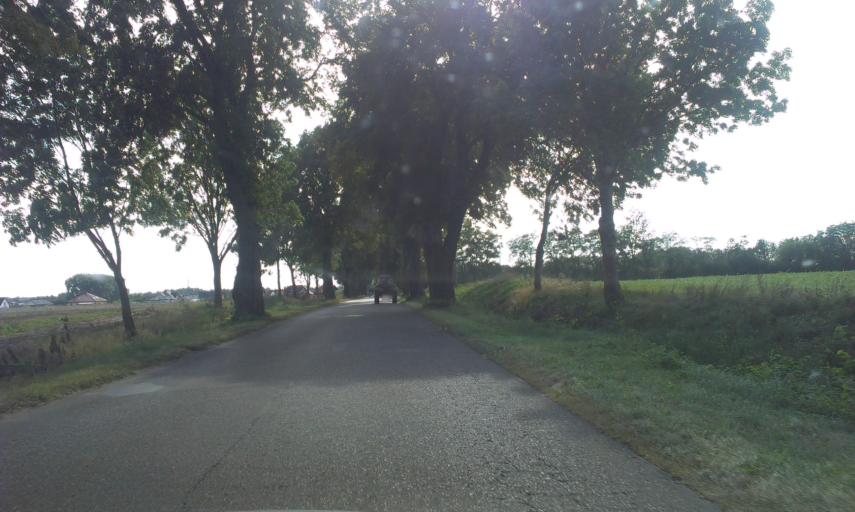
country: PL
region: Greater Poland Voivodeship
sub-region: Powiat zlotowski
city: Zlotow
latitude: 53.3801
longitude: 17.0187
